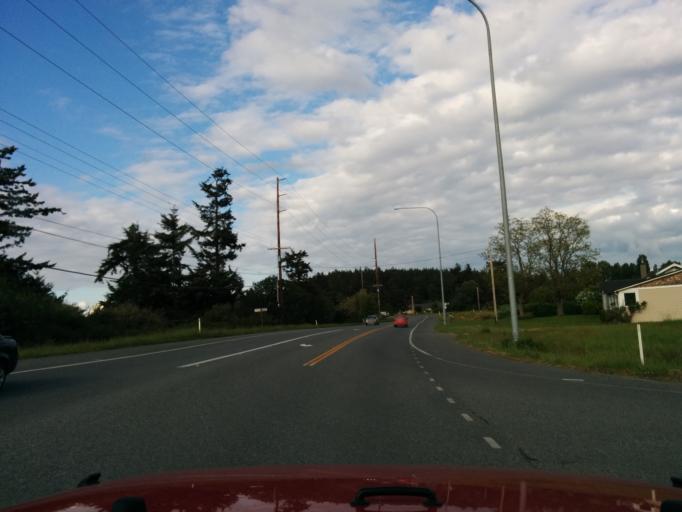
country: US
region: Washington
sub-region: Island County
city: Coupeville
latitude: 48.2645
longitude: -122.6807
